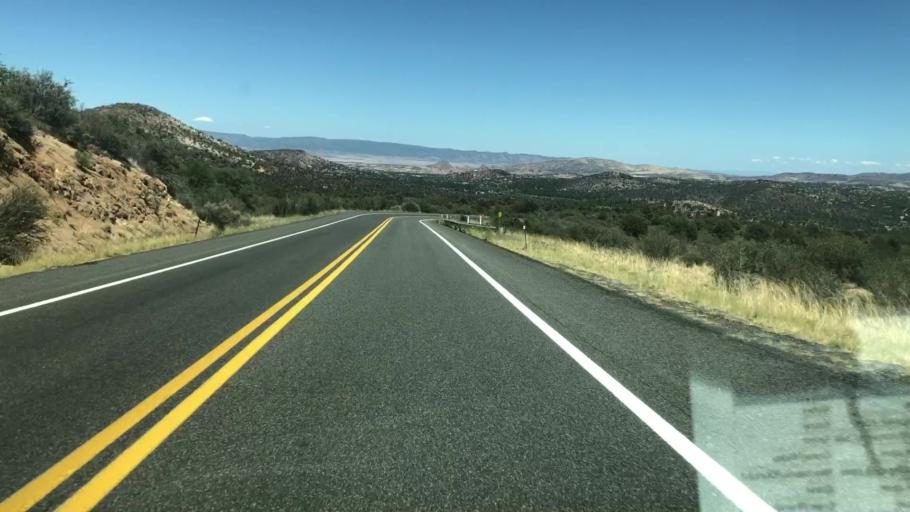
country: US
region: Arizona
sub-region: Yavapai County
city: Prescott
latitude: 34.5814
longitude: -112.5452
